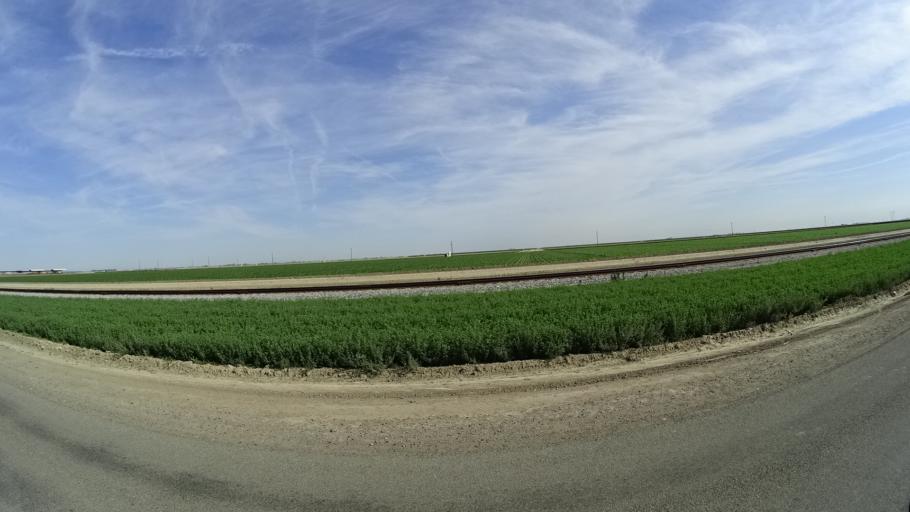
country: US
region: California
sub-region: Tulare County
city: Goshen
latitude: 36.3490
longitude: -119.4885
